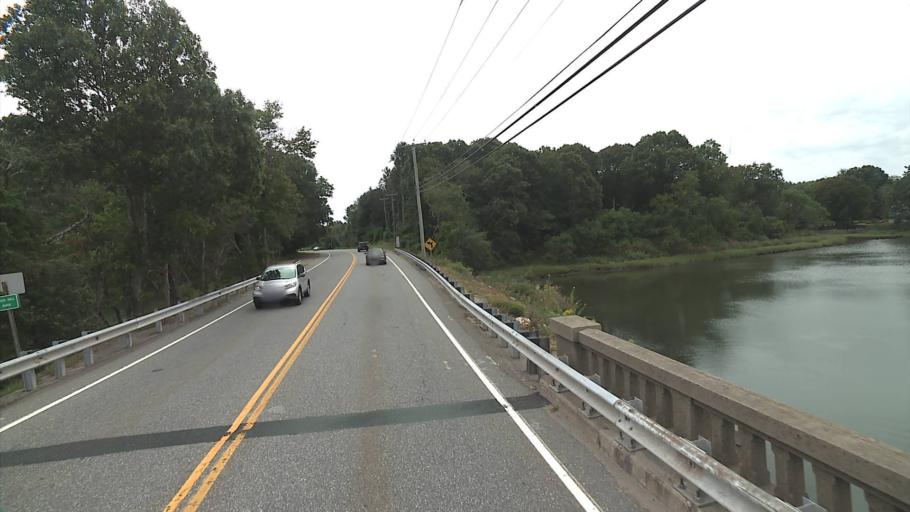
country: US
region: Connecticut
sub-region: Middlesex County
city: Old Saybrook Center
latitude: 41.2896
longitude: -72.3122
